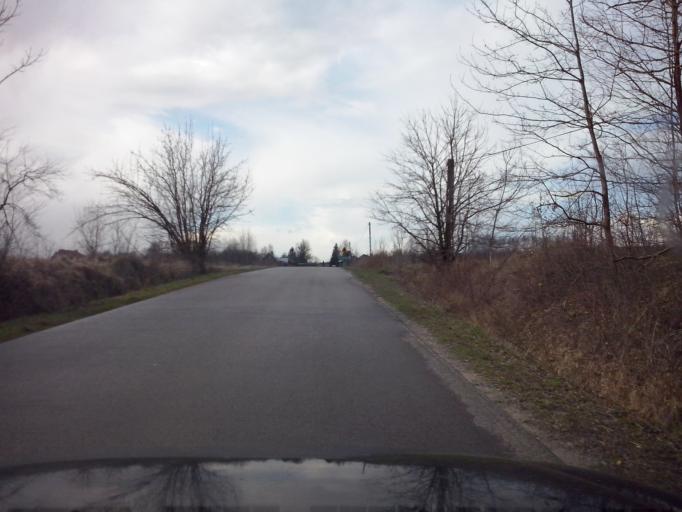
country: PL
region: Subcarpathian Voivodeship
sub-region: Powiat nizanski
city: Krzeszow
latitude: 50.4201
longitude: 22.3273
